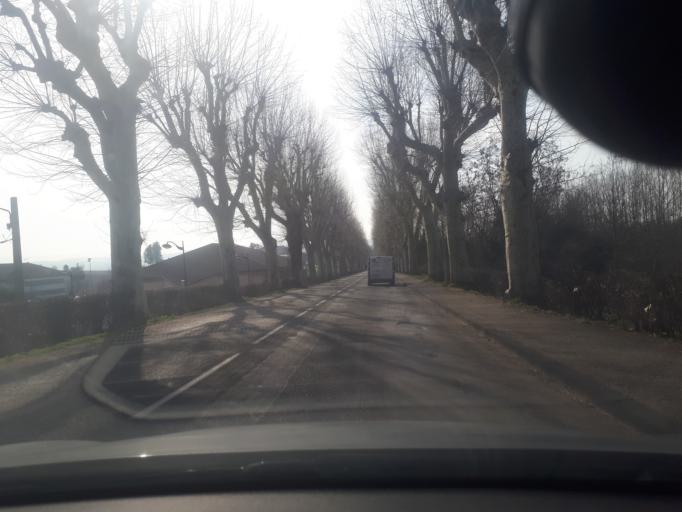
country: FR
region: Rhone-Alpes
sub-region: Departement de l'Isere
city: La Cote-Saint-Andre
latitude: 45.3911
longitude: 5.2615
